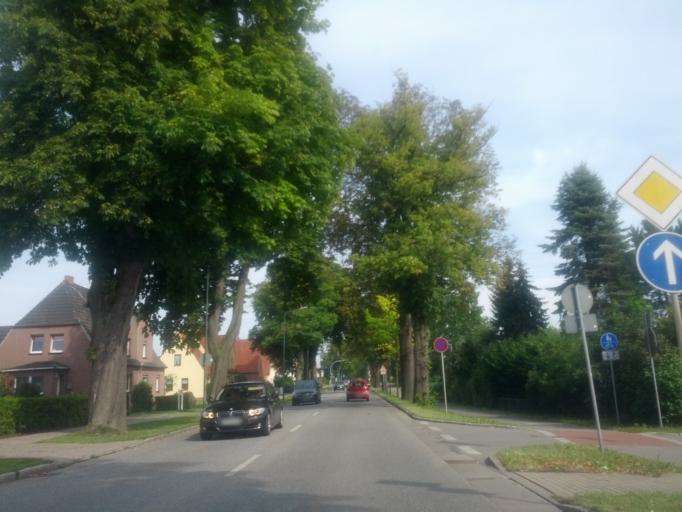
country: DE
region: Mecklenburg-Vorpommern
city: Hornstorf
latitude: 53.8927
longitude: 11.5031
